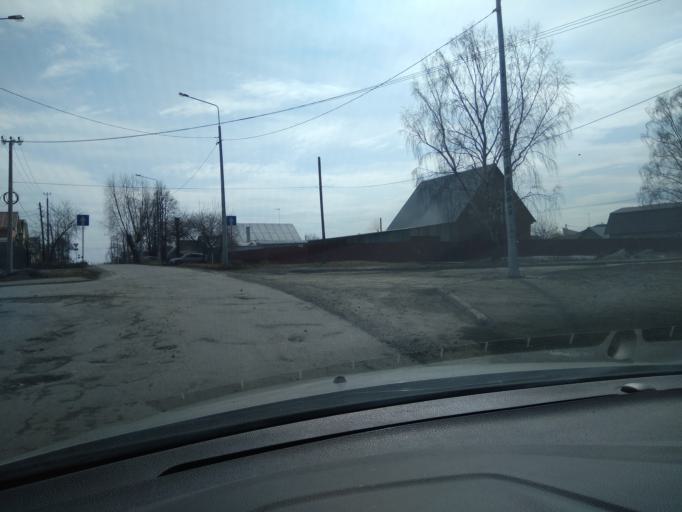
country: RU
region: Sverdlovsk
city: Shuvakish
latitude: 56.8924
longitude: 60.4847
